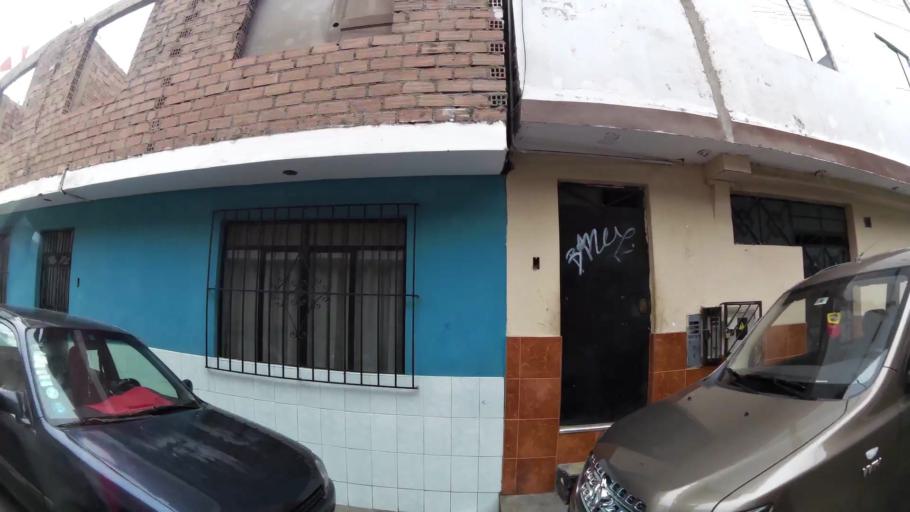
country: PE
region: Lima
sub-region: Lima
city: Surco
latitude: -12.1480
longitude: -77.0131
